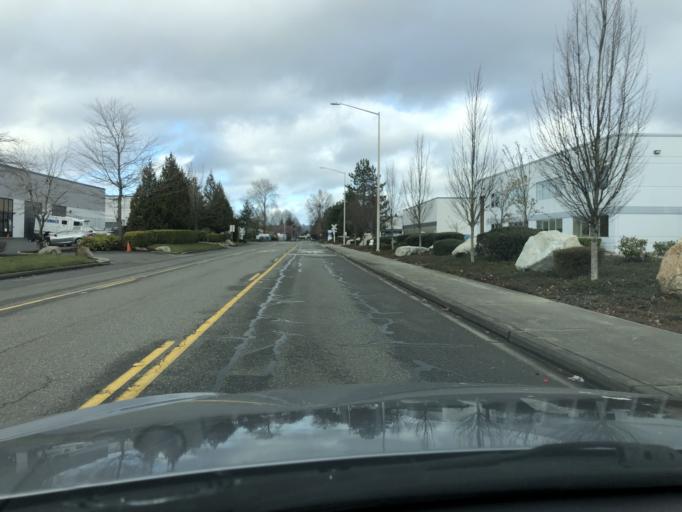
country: US
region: Washington
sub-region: King County
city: Tukwila
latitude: 47.4346
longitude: -122.2439
